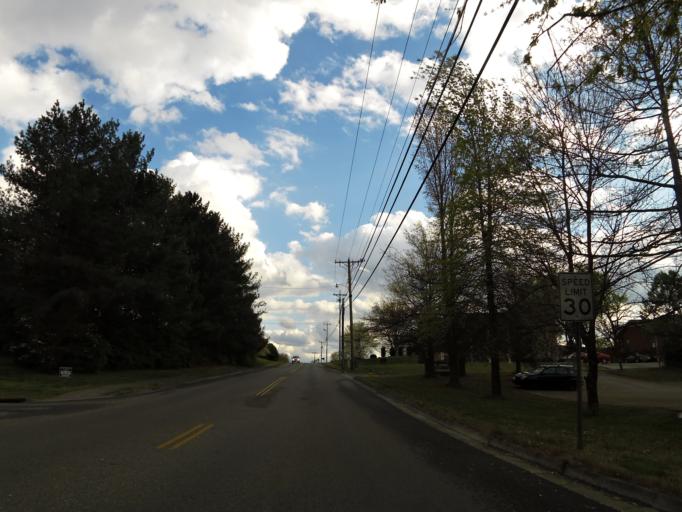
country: US
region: Tennessee
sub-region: Blount County
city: Maryville
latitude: 35.7324
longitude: -83.9790
